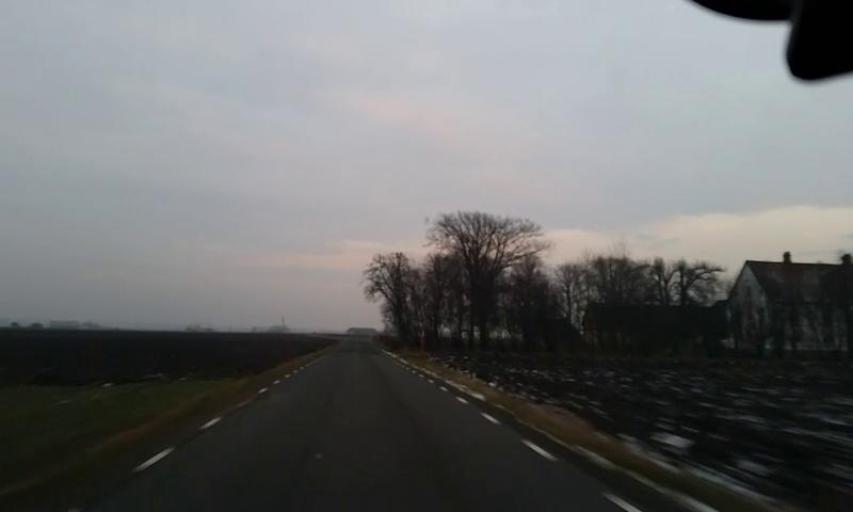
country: SE
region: Skane
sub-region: Angelholms Kommun
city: AEngelholm
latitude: 56.2755
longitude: 12.8781
